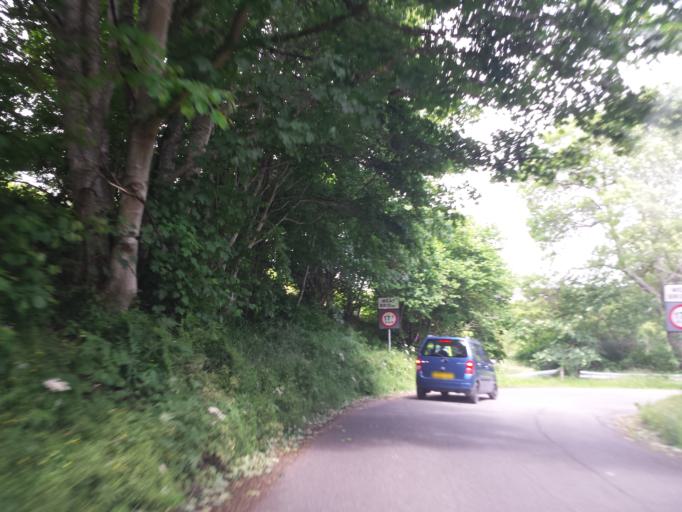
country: GB
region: Scotland
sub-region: Highland
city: Fortrose
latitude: 57.4768
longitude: -4.0714
